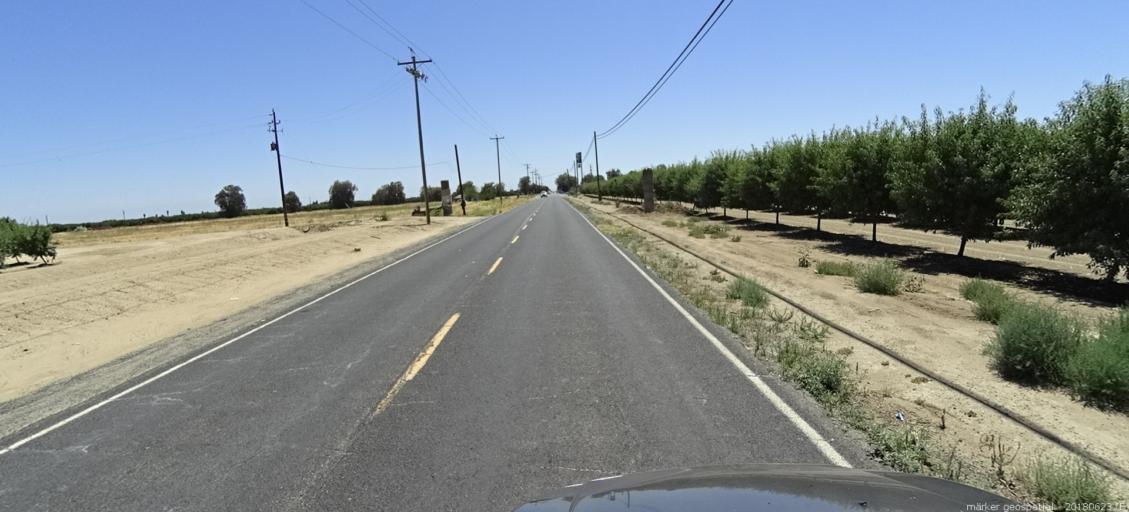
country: US
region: California
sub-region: Madera County
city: Fairmead
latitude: 37.0982
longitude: -120.2208
